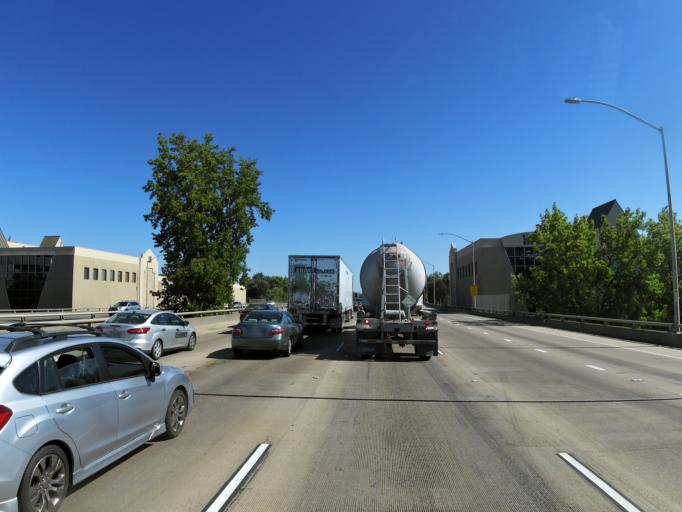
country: US
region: California
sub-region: Sacramento County
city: Sacramento
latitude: 38.5717
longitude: -121.4678
